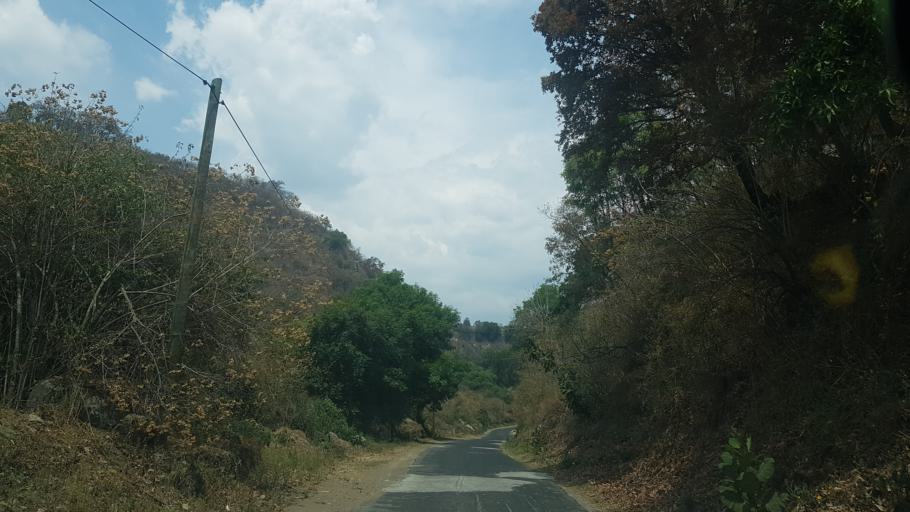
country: MX
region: Puebla
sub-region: Tochimilco
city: La Magdalena Yancuitlalpan
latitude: 18.8741
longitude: -98.6098
